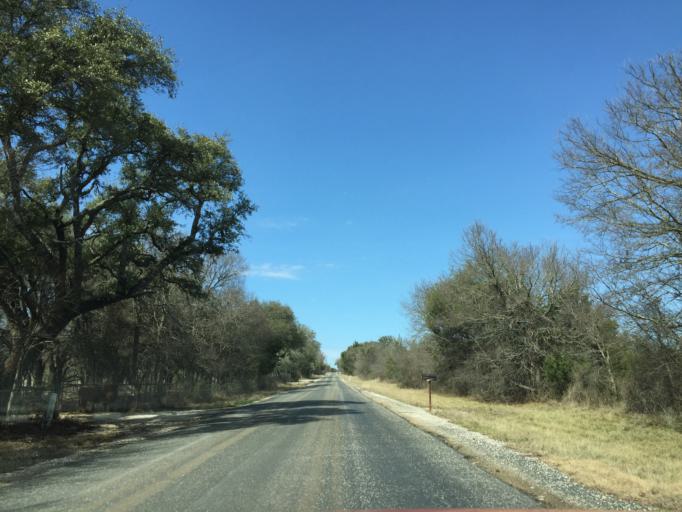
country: US
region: Texas
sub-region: Burnet County
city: Bertram
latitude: 30.7609
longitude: -97.9378
